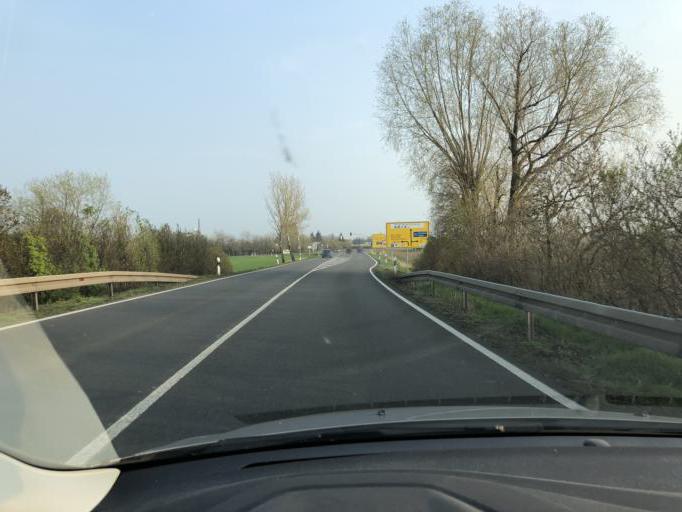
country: DE
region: Saxony
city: Delitzsch
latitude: 51.5262
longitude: 12.3106
